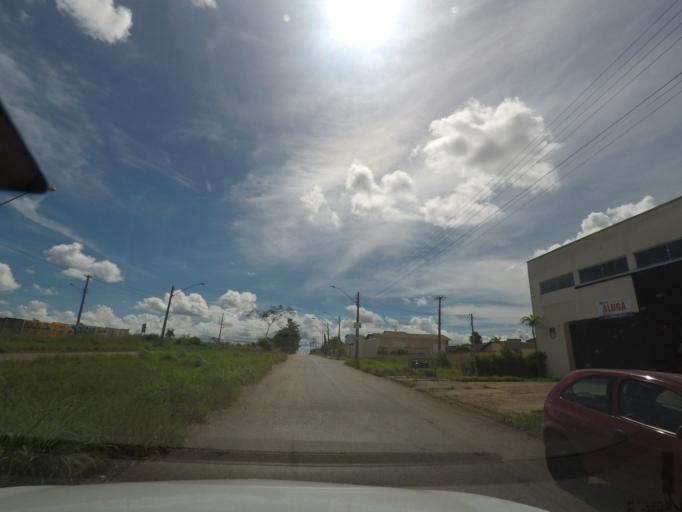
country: BR
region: Goias
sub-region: Goiania
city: Goiania
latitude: -16.7440
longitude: -49.3406
